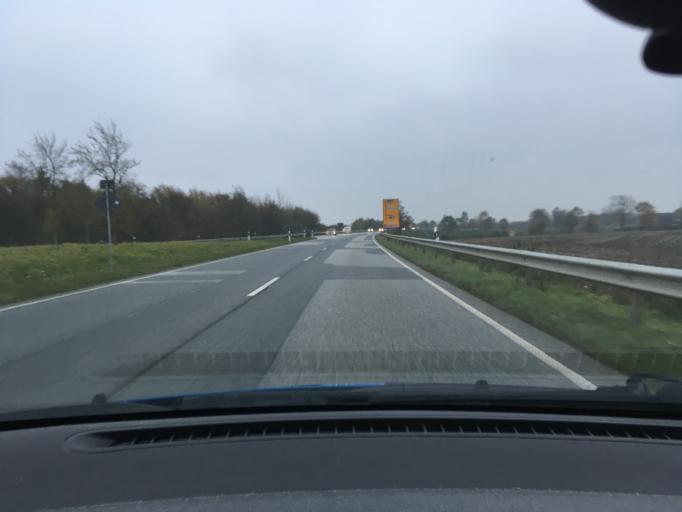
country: DE
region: Schleswig-Holstein
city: Mildstedt
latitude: 54.4879
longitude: 9.0927
